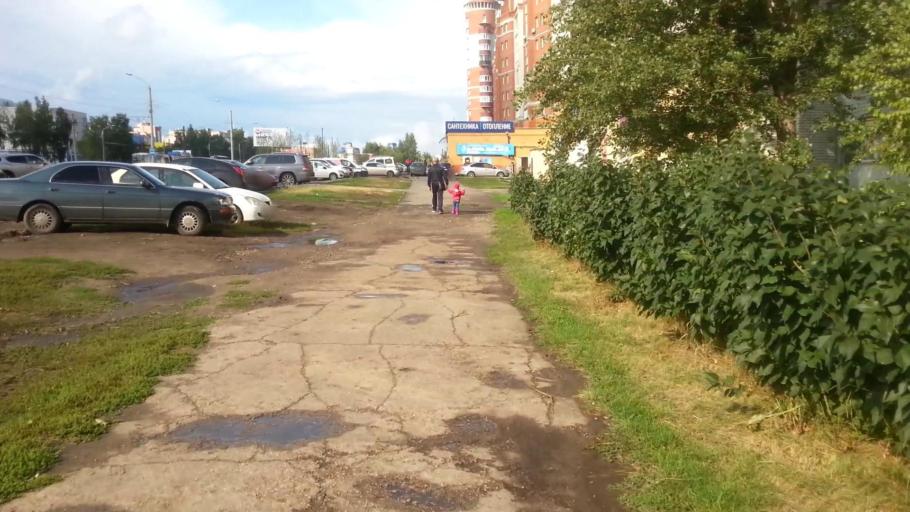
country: RU
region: Altai Krai
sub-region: Gorod Barnaulskiy
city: Barnaul
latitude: 53.3512
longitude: 83.6982
